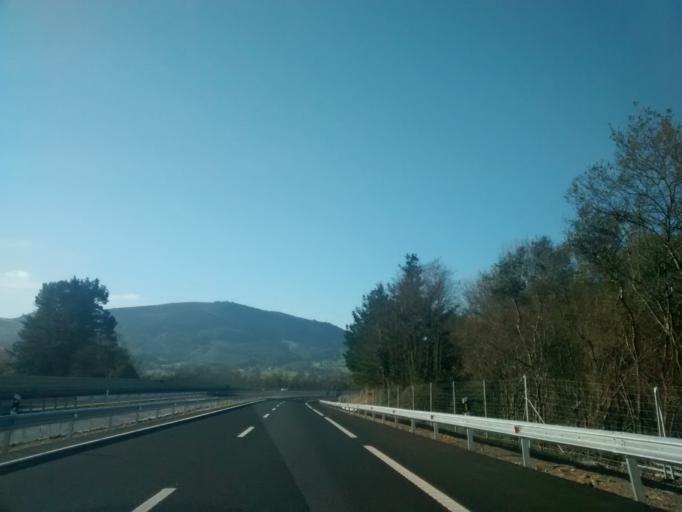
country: ES
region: Cantabria
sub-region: Provincia de Cantabria
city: Santa Maria de Cayon
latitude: 43.3242
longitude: -3.8594
